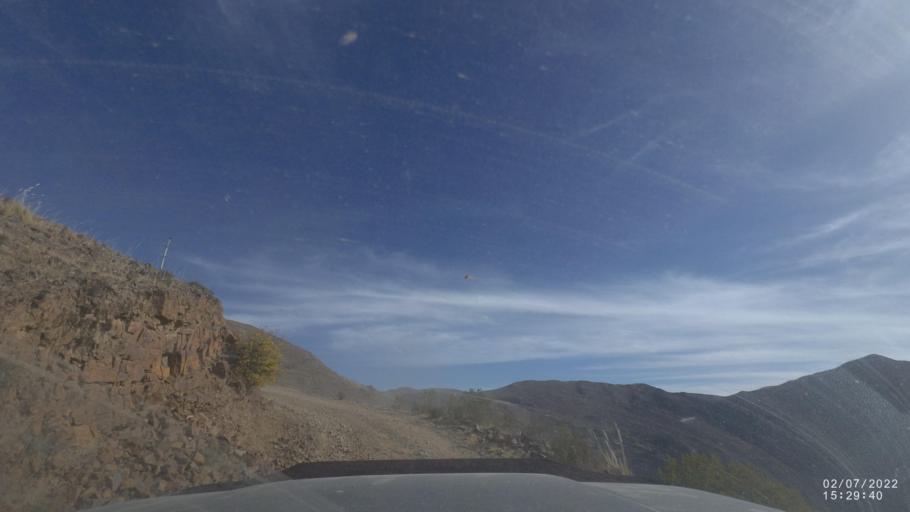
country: BO
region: Cochabamba
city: Irpa Irpa
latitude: -17.8794
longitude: -66.4139
